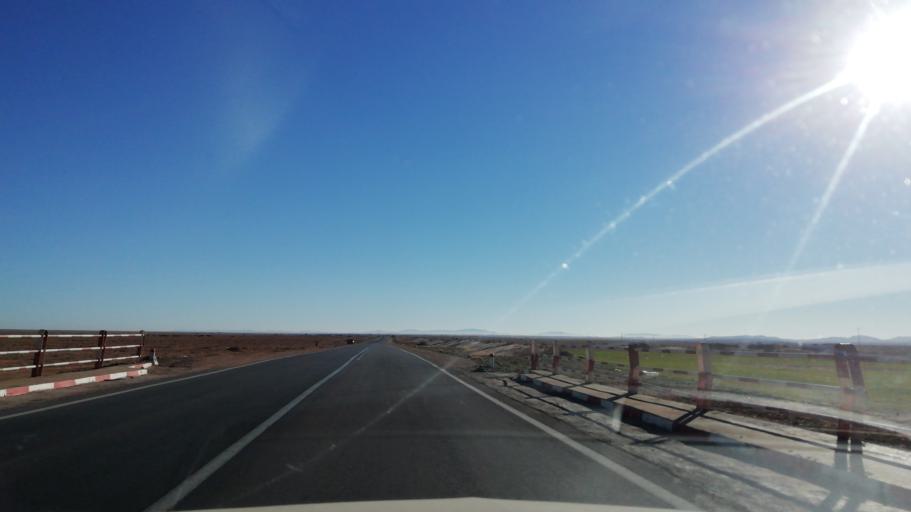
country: DZ
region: El Bayadh
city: El Bayadh
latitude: 33.8586
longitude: 0.5704
